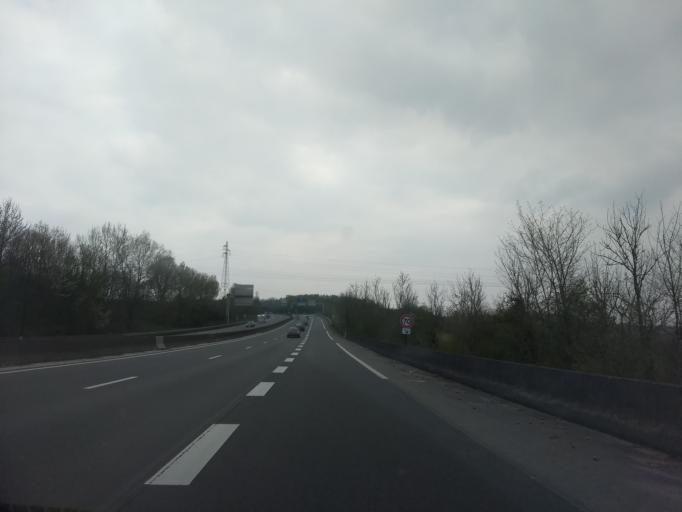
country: FR
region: Nord-Pas-de-Calais
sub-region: Departement du Pas-de-Calais
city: Saint-Nicolas
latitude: 50.3149
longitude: 2.7749
